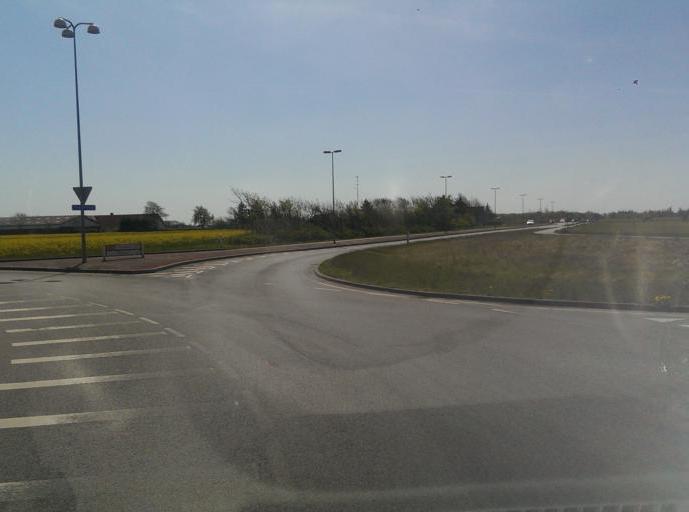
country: DK
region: South Denmark
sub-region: Esbjerg Kommune
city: Ribe
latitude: 55.3158
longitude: 8.7512
